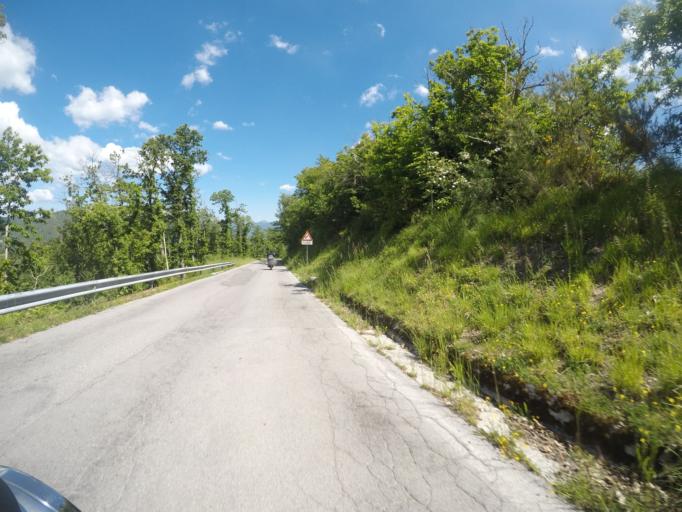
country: IT
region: Tuscany
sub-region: Provincia di Lucca
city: Careggine
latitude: 44.1240
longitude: 10.3302
